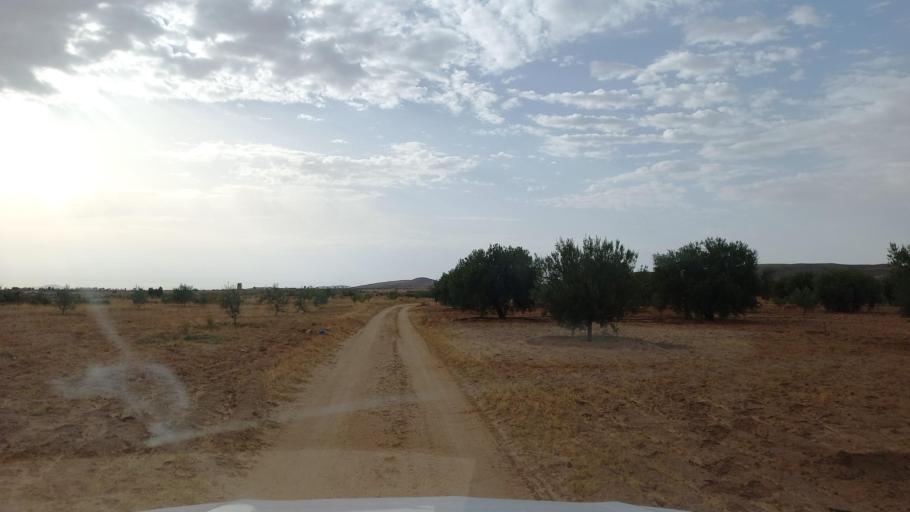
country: TN
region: Al Qasrayn
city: Kasserine
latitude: 35.1901
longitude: 9.0506
